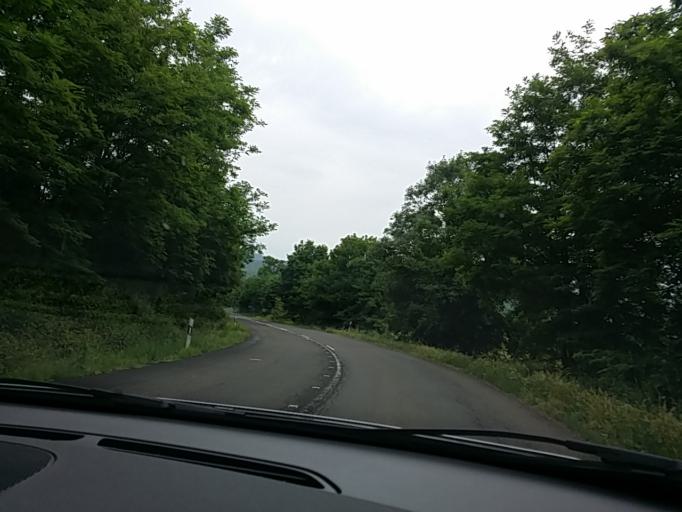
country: HU
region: Nograd
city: Matranovak
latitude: 48.0056
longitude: 20.0059
